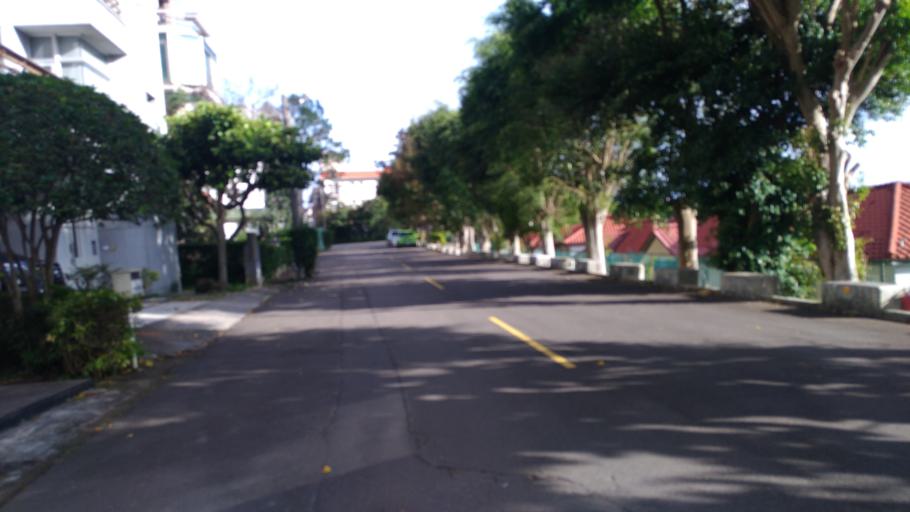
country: TW
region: Taiwan
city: Daxi
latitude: 24.8848
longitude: 121.1695
